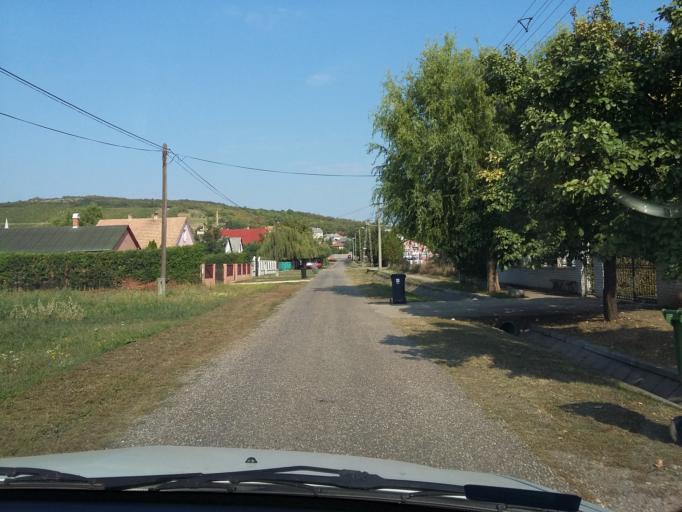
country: HU
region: Borsod-Abauj-Zemplen
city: Bekecs
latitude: 48.1502
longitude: 21.1791
